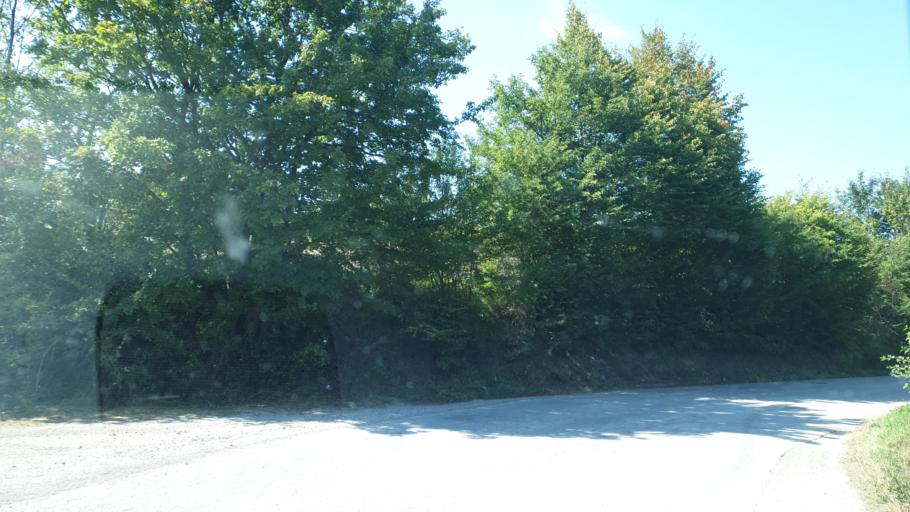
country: RS
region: Central Serbia
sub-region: Zlatiborski Okrug
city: Cajetina
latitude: 43.7012
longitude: 19.8479
